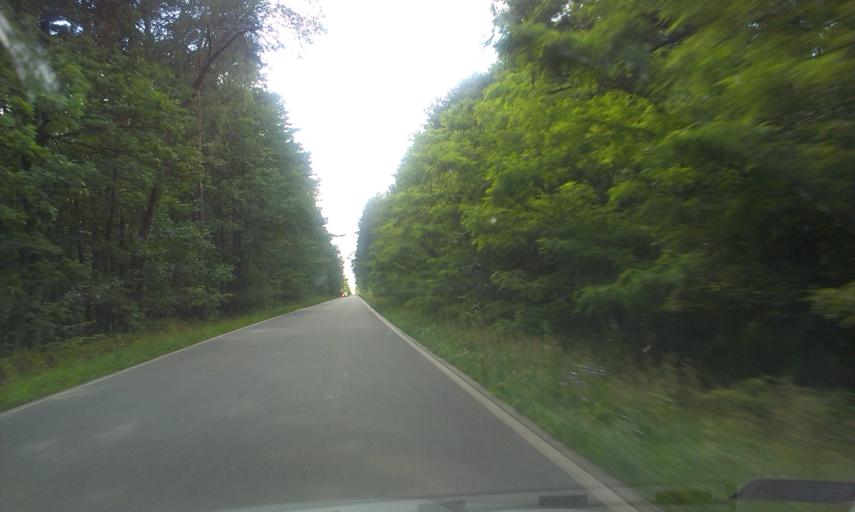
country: PL
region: Masovian Voivodeship
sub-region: Powiat zyrardowski
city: Radziejowice
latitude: 51.9667
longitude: 20.6067
